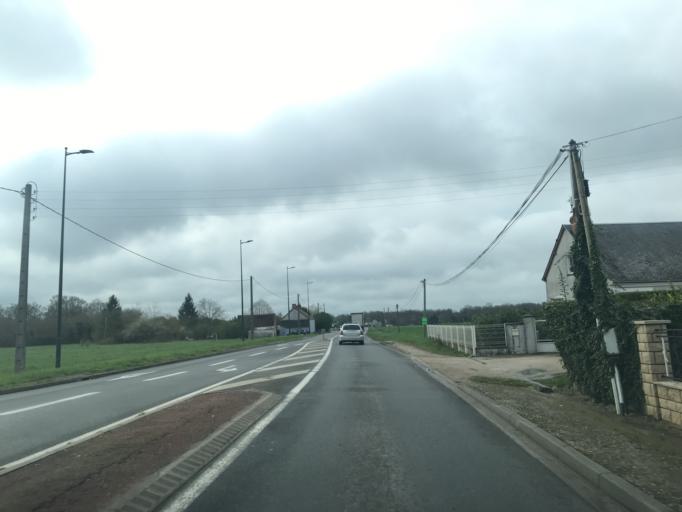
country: FR
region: Centre
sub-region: Departement du Loiret
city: Bray-en-Val
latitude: 47.8316
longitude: 2.3673
